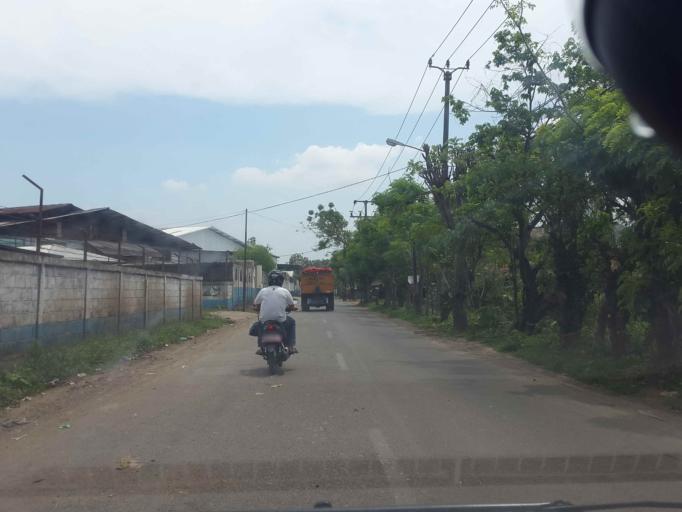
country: ID
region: Banten
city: Tangerang
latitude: -6.1415
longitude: 106.6178
